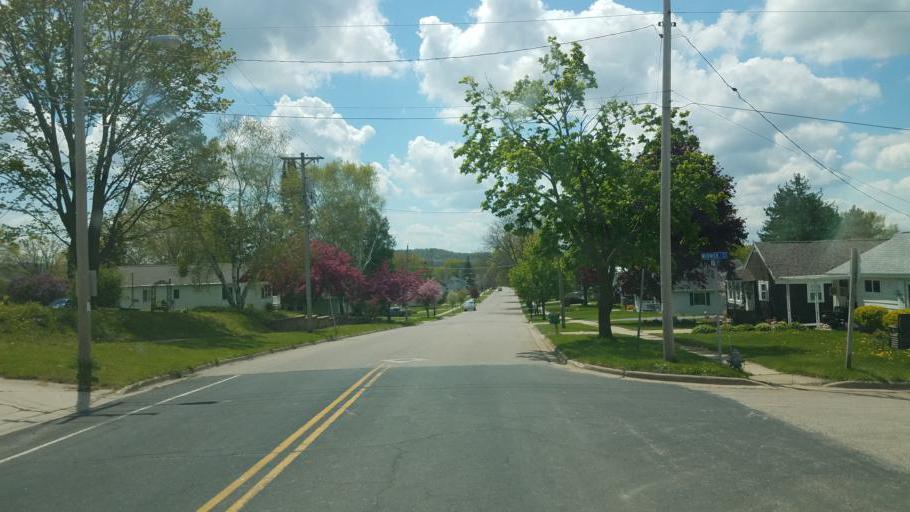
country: US
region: Wisconsin
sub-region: Vernon County
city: Hillsboro
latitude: 43.6585
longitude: -90.3455
